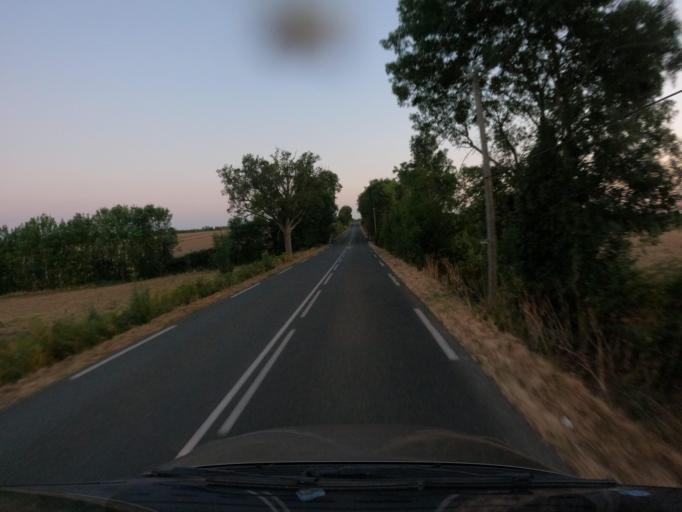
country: FR
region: Pays de la Loire
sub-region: Departement de Maine-et-Loire
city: Cande
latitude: 47.5776
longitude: -1.0151
